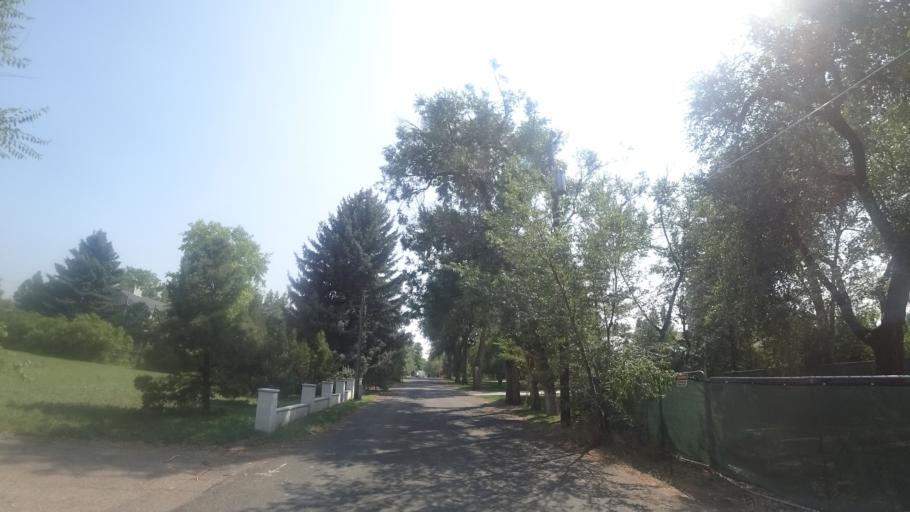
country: US
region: Colorado
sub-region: Arapahoe County
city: Cherry Hills Village
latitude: 39.6363
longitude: -104.9737
